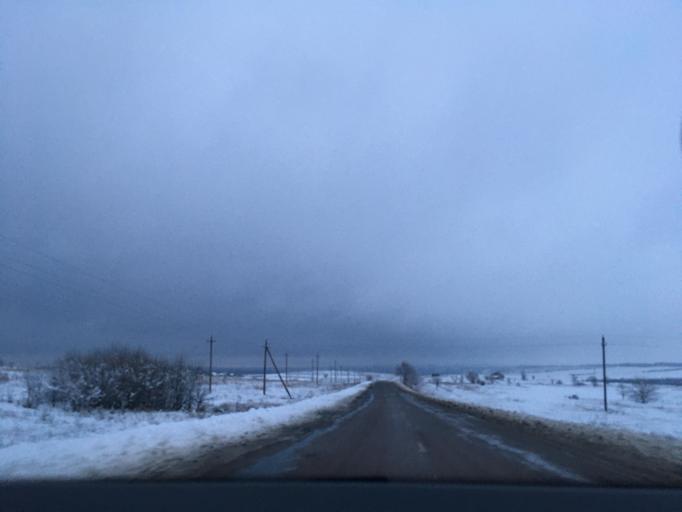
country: RU
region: Voronezj
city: Verkhniy Mamon
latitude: 50.0726
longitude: 40.2976
